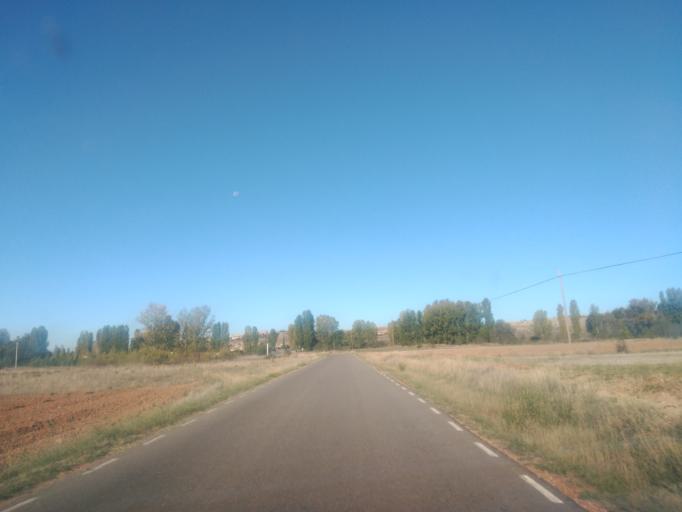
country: ES
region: Castille and Leon
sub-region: Provincia de Burgos
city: Penaranda de Duero
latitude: 41.6874
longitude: -3.4584
